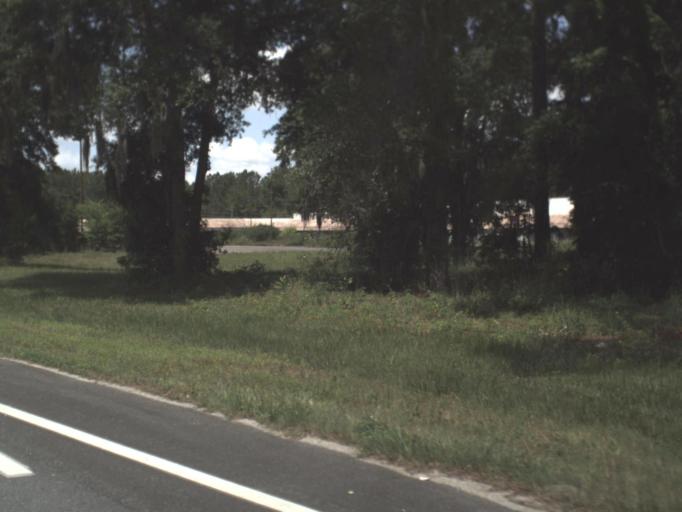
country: US
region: Florida
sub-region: Levy County
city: Williston
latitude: 29.4028
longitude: -82.4389
